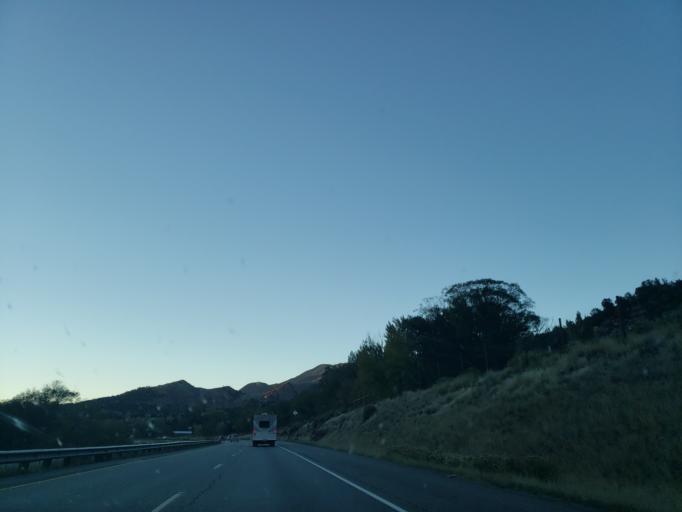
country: US
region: Colorado
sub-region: Garfield County
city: New Castle
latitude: 39.5738
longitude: -107.4352
